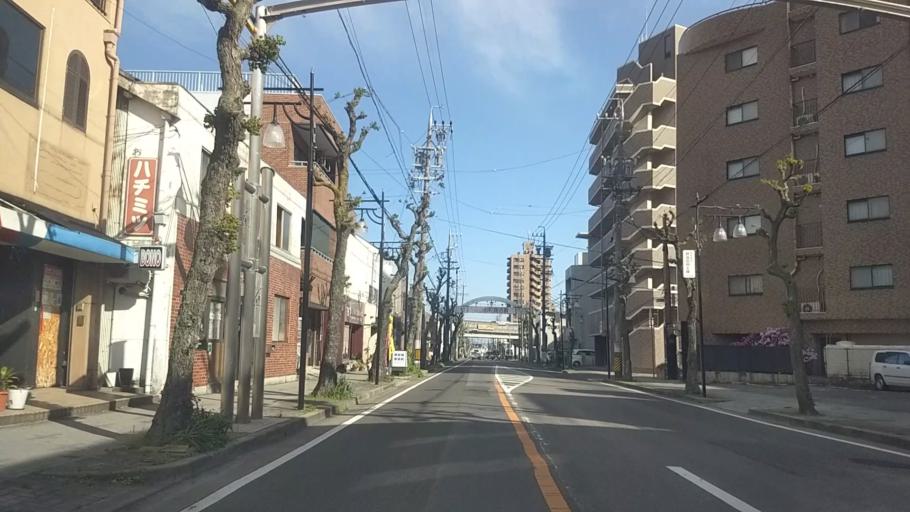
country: JP
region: Aichi
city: Anjo
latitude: 34.9540
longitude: 137.0913
